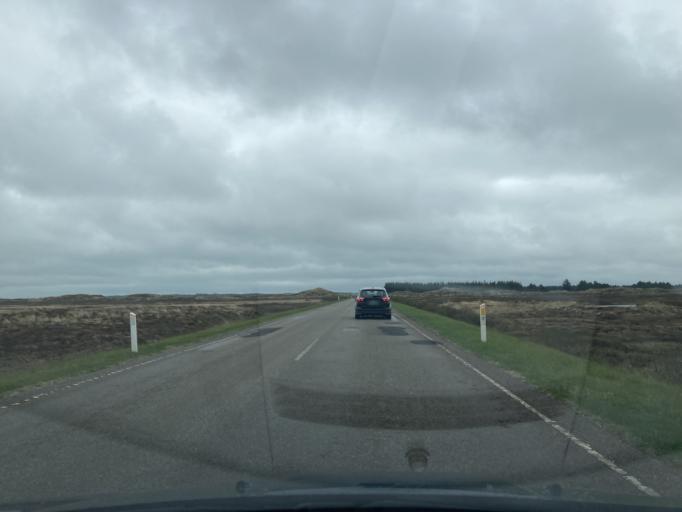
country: DK
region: North Denmark
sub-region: Thisted Kommune
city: Hanstholm
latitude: 57.0137
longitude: 8.4715
